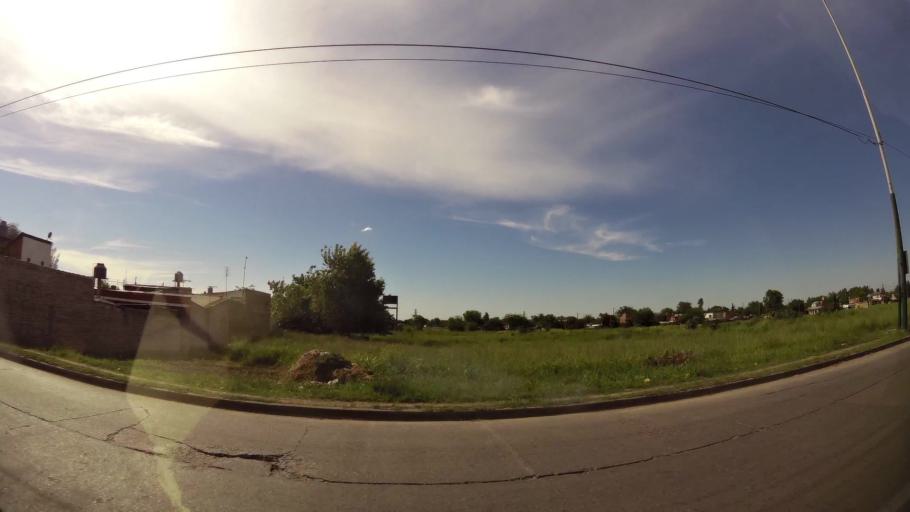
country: AR
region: Buenos Aires
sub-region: Partido de Almirante Brown
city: Adrogue
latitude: -34.8139
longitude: -58.3528
